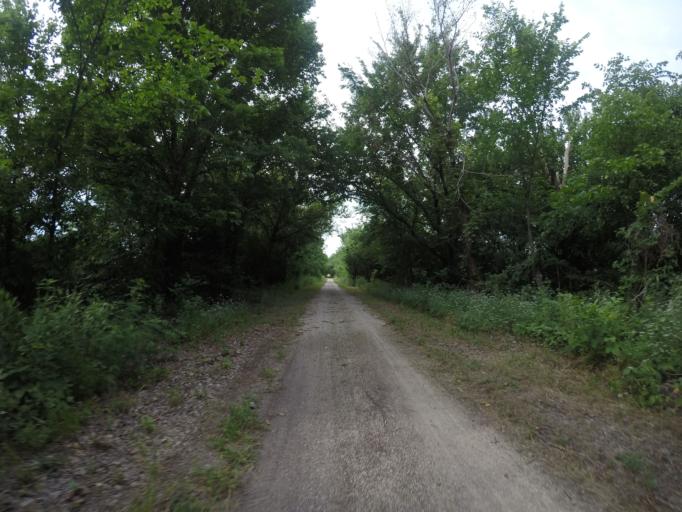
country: US
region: Kansas
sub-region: Franklin County
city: Ottawa
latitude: 38.5026
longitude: -95.2732
